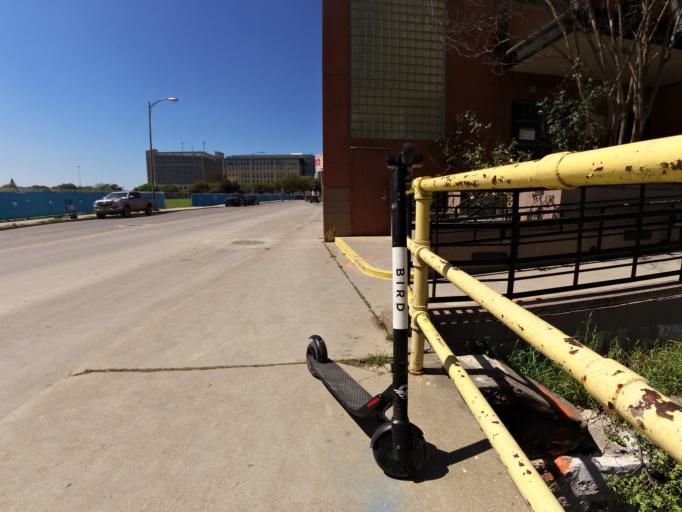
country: US
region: Texas
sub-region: Bexar County
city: San Antonio
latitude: 29.4229
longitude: -98.4964
